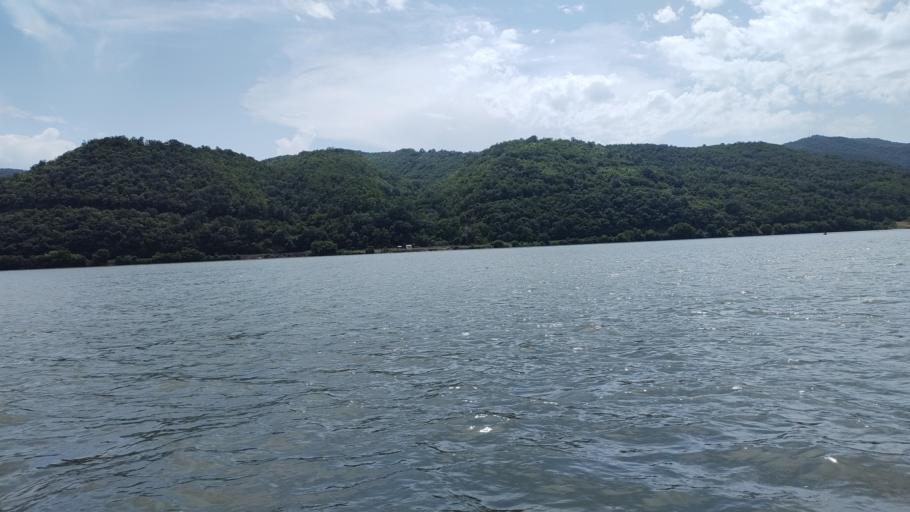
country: RO
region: Caras-Severin
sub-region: Comuna Berzasca
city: Berzasca
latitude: 44.6443
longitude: 21.9263
